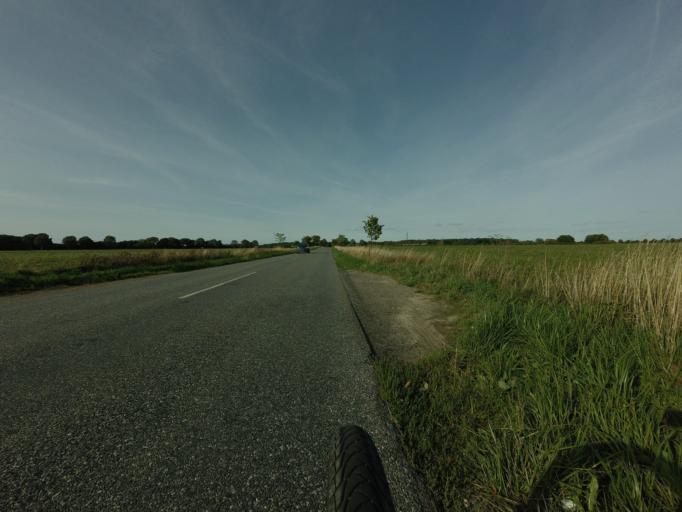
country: DK
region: Zealand
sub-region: Faxe Kommune
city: Fakse Ladeplads
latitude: 55.2465
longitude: 12.2201
